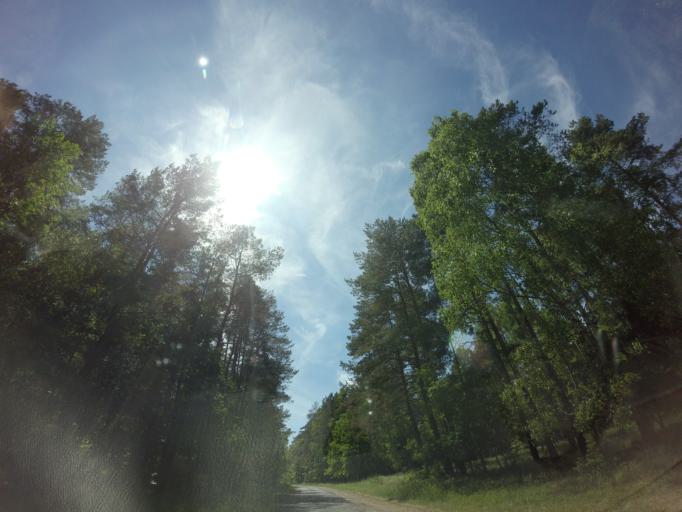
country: PL
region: West Pomeranian Voivodeship
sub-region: Powiat choszczenski
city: Drawno
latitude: 53.1440
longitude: 15.8668
